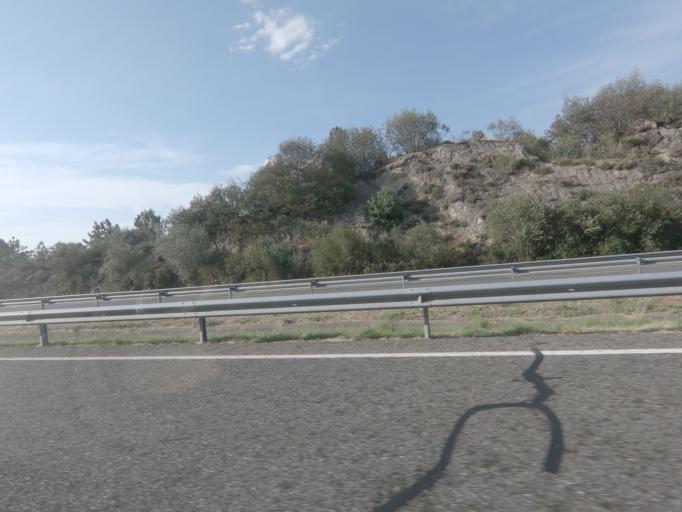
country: ES
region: Galicia
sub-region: Provincia de Ourense
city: Oimbra
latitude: 41.9233
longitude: -7.4813
